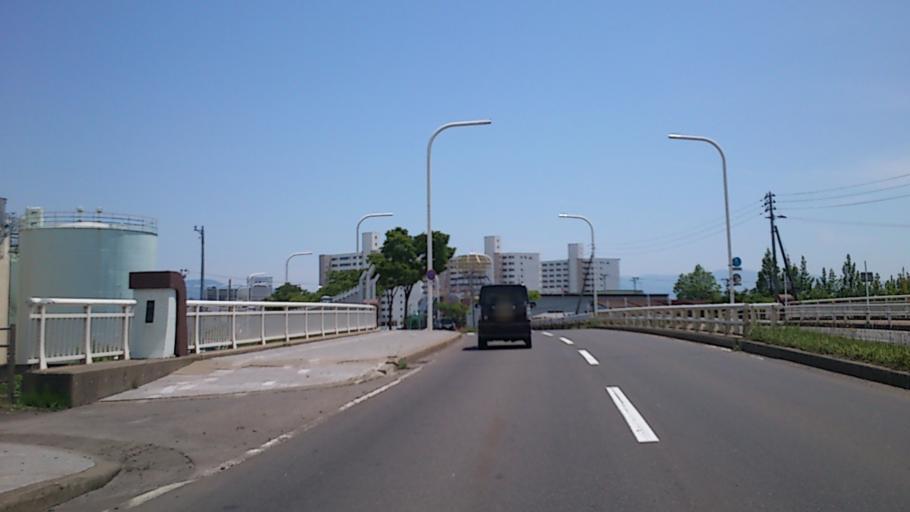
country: JP
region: Aomori
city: Aomori Shi
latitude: 40.8343
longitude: 140.7276
